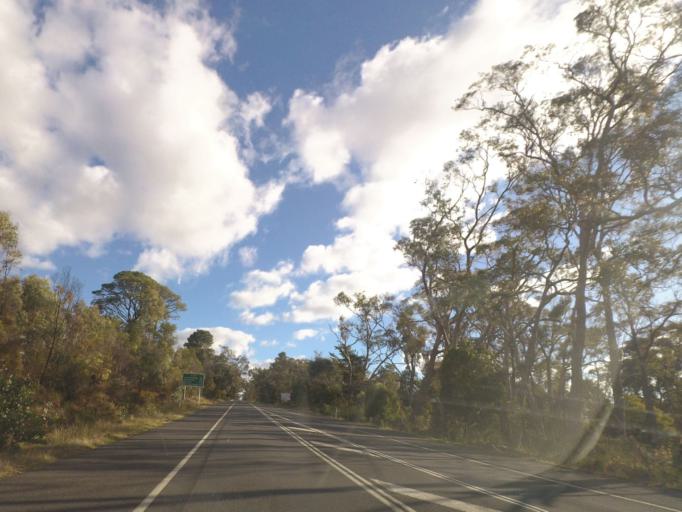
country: AU
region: Victoria
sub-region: Mount Alexander
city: Castlemaine
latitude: -37.1037
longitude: 144.3151
